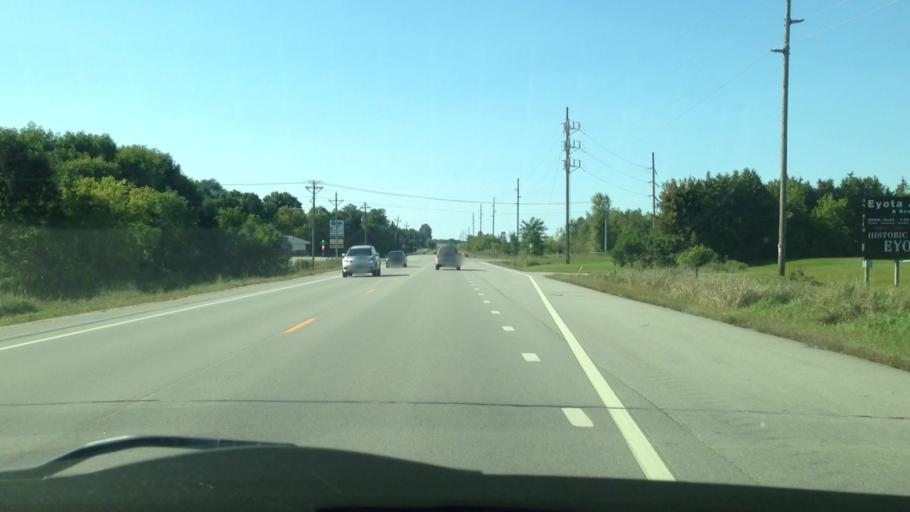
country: US
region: Minnesota
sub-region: Olmsted County
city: Eyota
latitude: 43.9905
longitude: -92.2275
